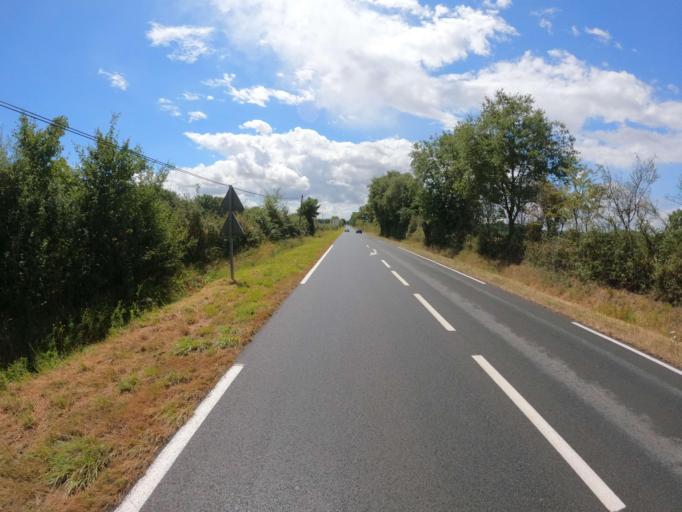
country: FR
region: Pays de la Loire
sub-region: Departement de Maine-et-Loire
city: Feneu
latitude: 47.6108
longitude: -0.5855
